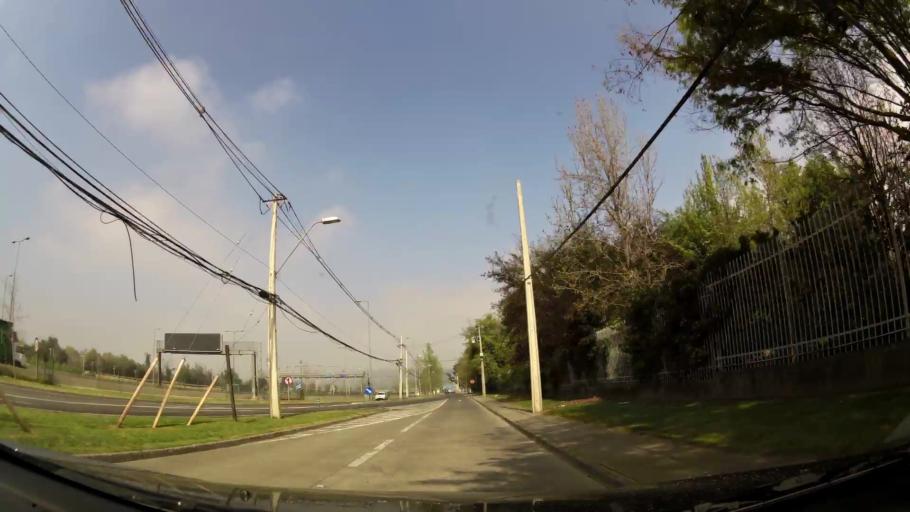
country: CL
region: Santiago Metropolitan
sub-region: Provincia de Santiago
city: Villa Presidente Frei, Nunoa, Santiago, Chile
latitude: -33.3837
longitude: -70.5920
